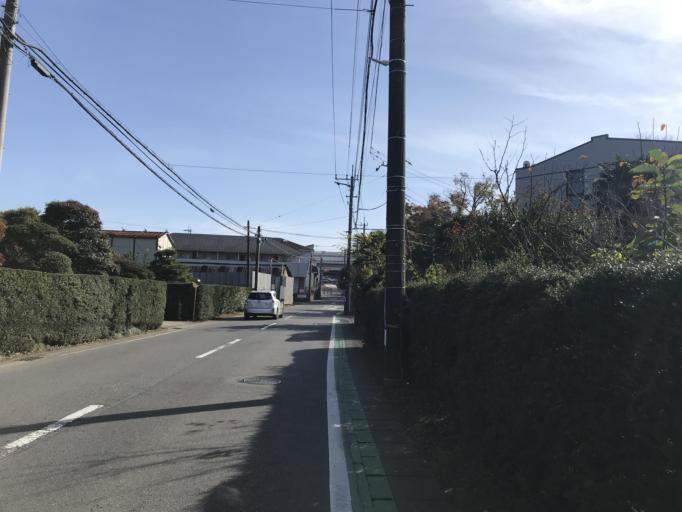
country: JP
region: Chiba
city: Shiroi
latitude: 35.7793
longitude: 139.9913
